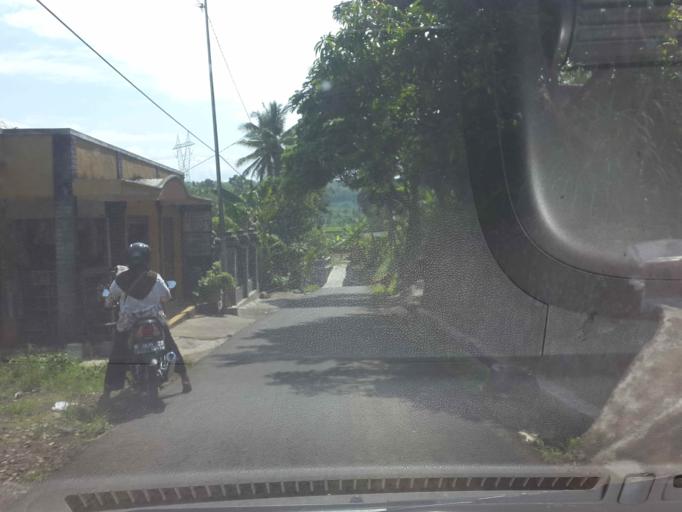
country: ID
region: Central Java
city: Salatiga
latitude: -7.3352
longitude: 110.5236
